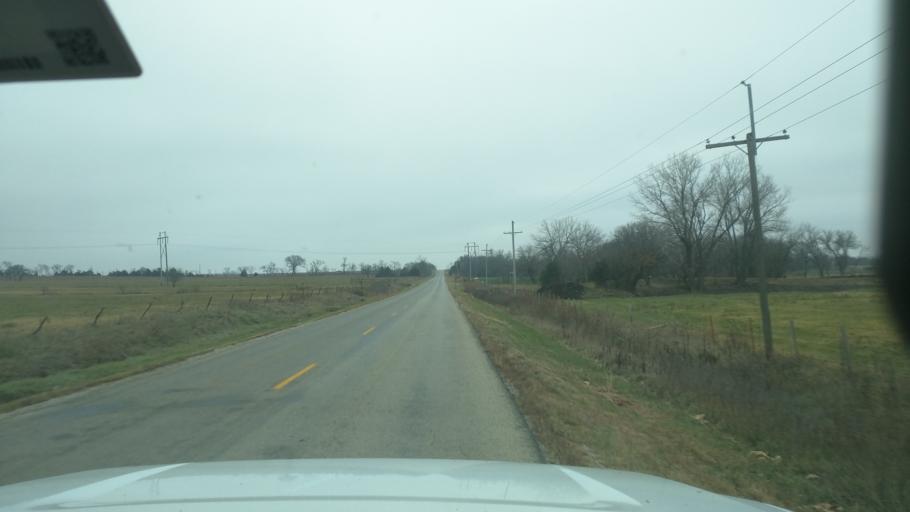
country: US
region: Kansas
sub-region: Lyon County
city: Emporia
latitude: 38.5629
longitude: -96.2612
